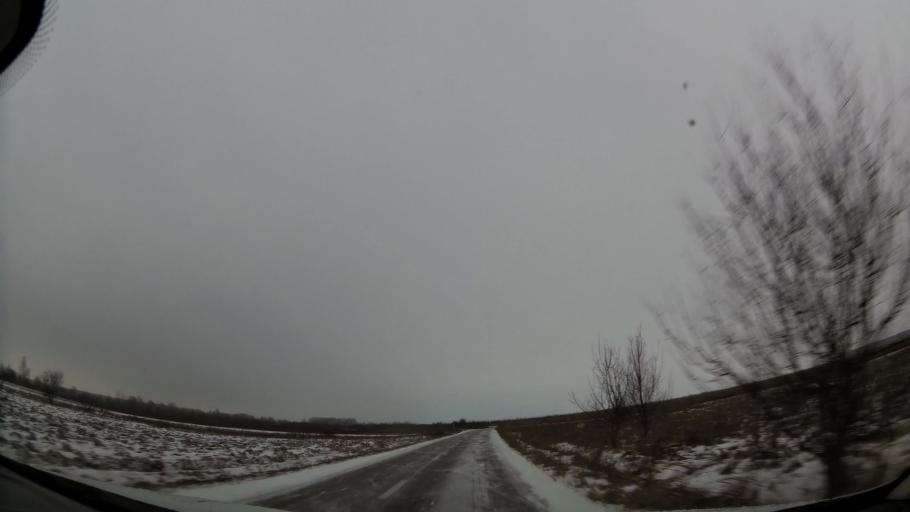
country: RO
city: Fantanele
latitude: 44.7334
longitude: 25.9043
